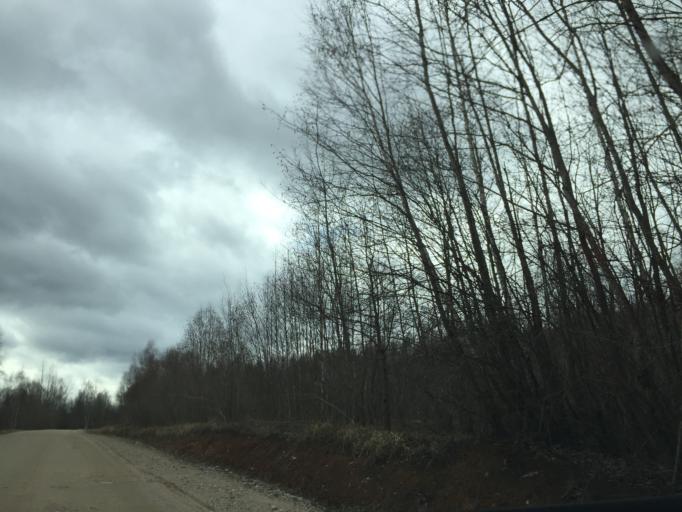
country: LV
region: Kraslavas Rajons
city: Kraslava
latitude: 55.9468
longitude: 26.9944
